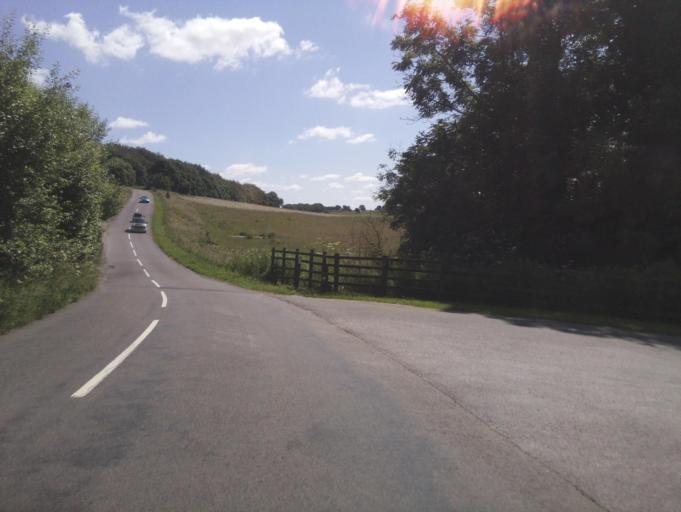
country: GB
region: England
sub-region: Derbyshire
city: Tideswell
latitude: 53.1906
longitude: -1.8099
